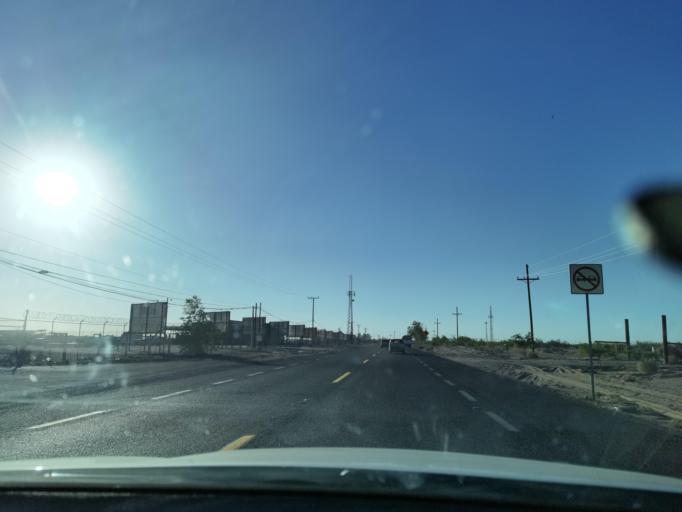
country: MX
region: Baja California
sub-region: Mexicali
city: Islas Agrarias Grupo A
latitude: 32.6308
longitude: -115.2602
